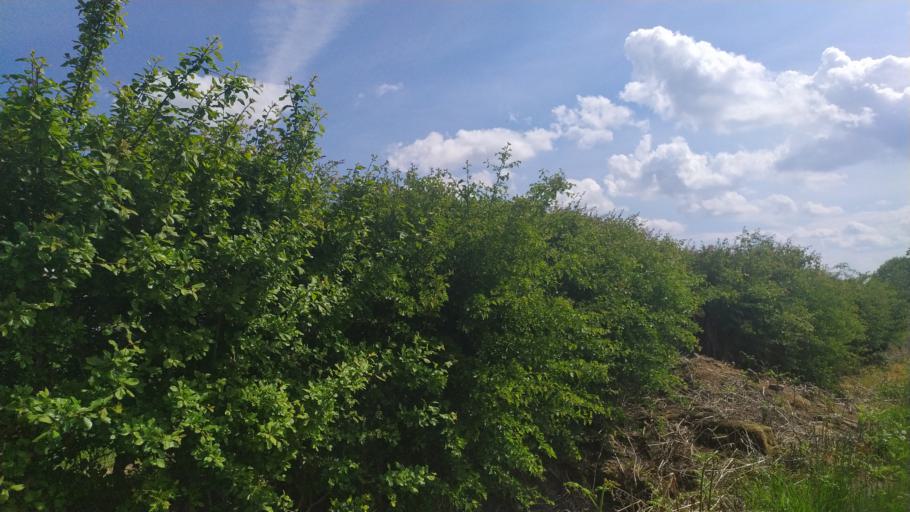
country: GB
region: England
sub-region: City and Borough of Leeds
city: Chapel Allerton
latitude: 53.8796
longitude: -1.5584
